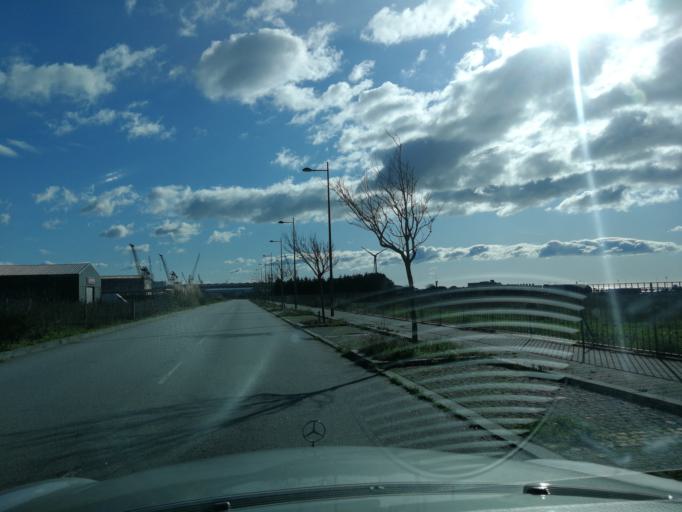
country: PT
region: Viana do Castelo
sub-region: Viana do Castelo
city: Viana do Castelo
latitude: 41.6983
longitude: -8.8480
